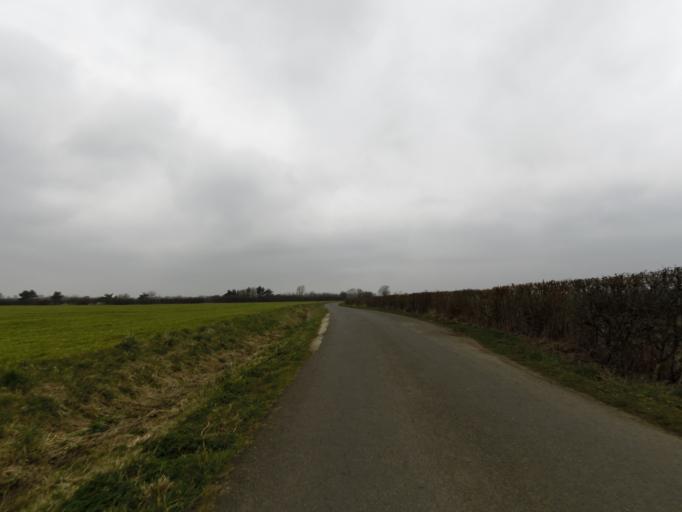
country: GB
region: England
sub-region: Suffolk
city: Framlingham
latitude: 52.2336
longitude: 1.3792
